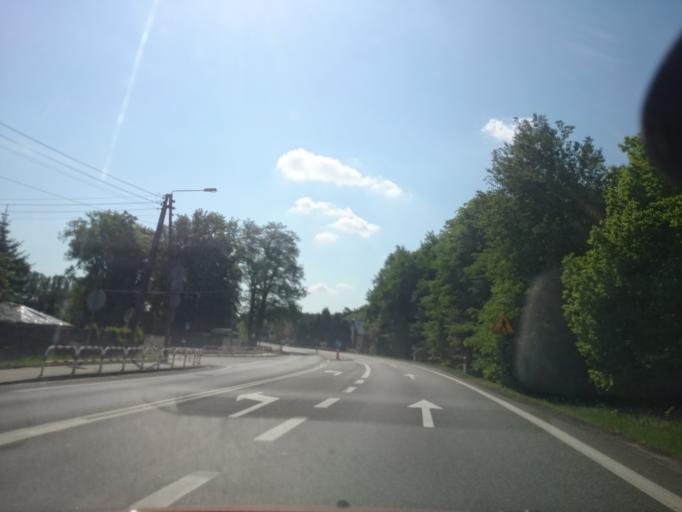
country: PL
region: Opole Voivodeship
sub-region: Powiat opolski
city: Tarnow Opolski
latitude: 50.6049
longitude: 18.0751
